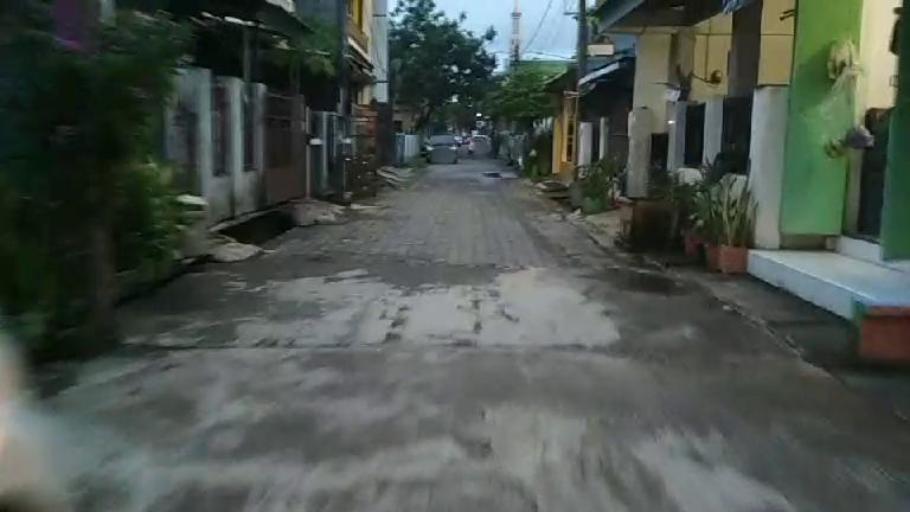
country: ID
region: South Sulawesi
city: Makassar
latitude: -5.1392
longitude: 119.5059
